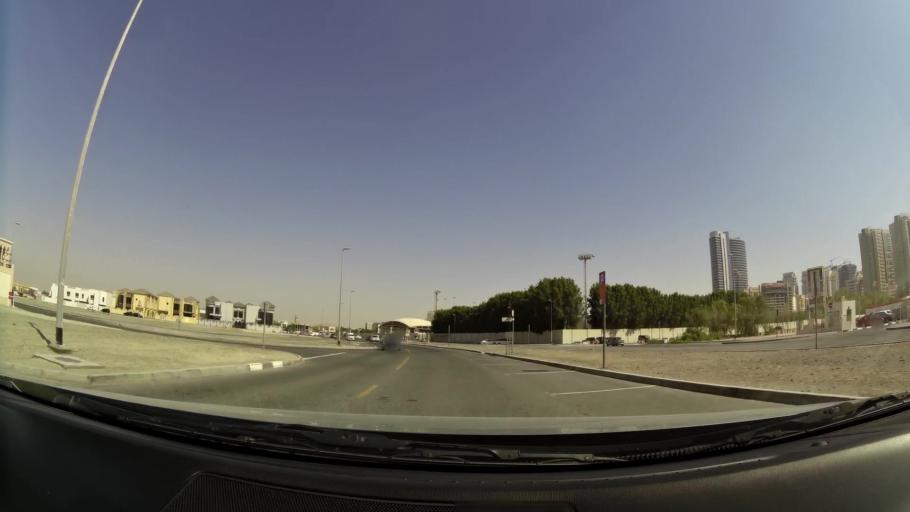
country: AE
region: Dubai
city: Dubai
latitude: 25.1033
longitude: 55.1825
